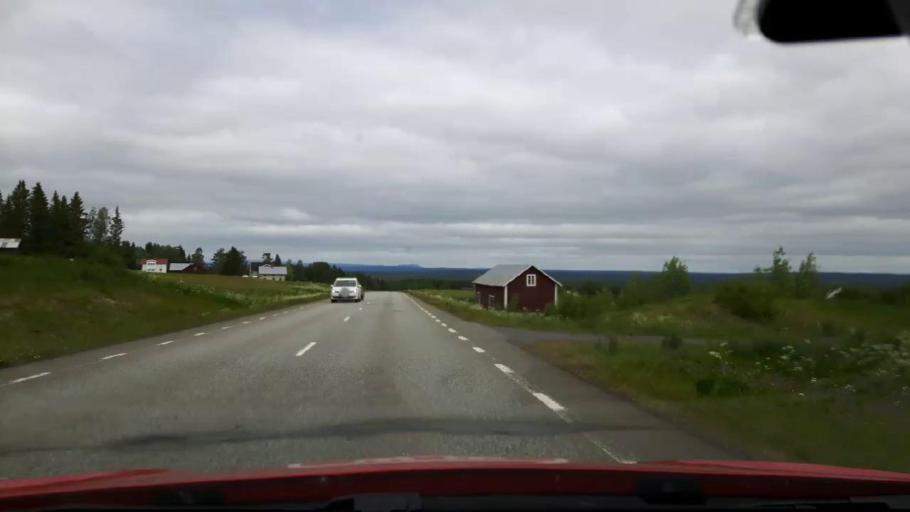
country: SE
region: Jaemtland
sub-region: Krokoms Kommun
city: Krokom
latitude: 63.5791
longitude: 14.6336
